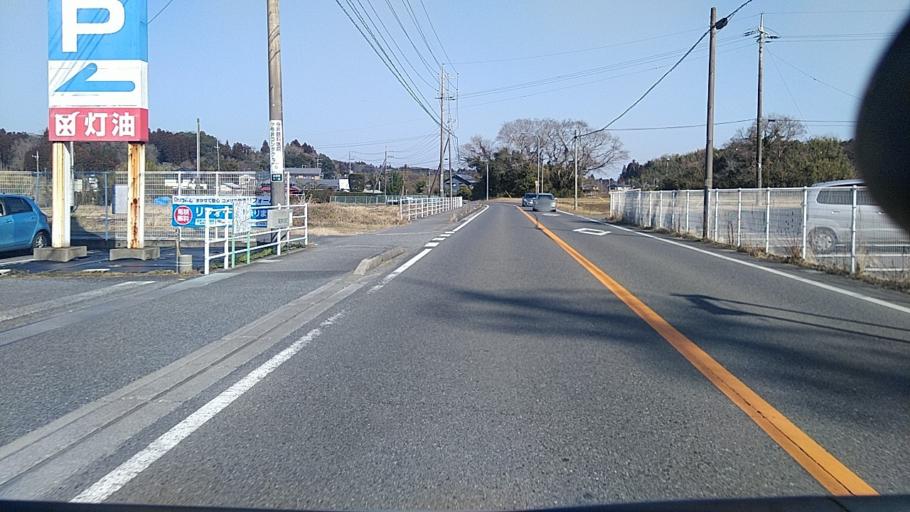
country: JP
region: Chiba
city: Mobara
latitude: 35.4067
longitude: 140.2401
